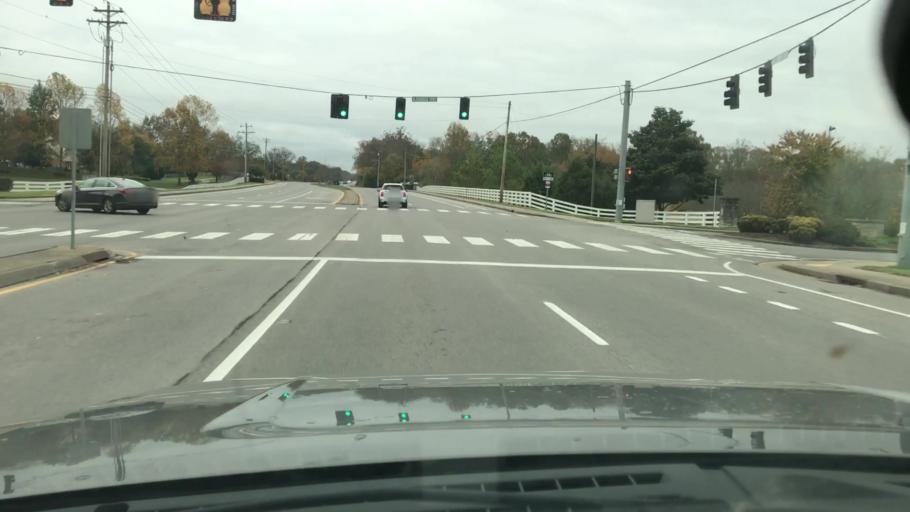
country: US
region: Tennessee
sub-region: Williamson County
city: Franklin
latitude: 35.9591
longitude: -86.8847
